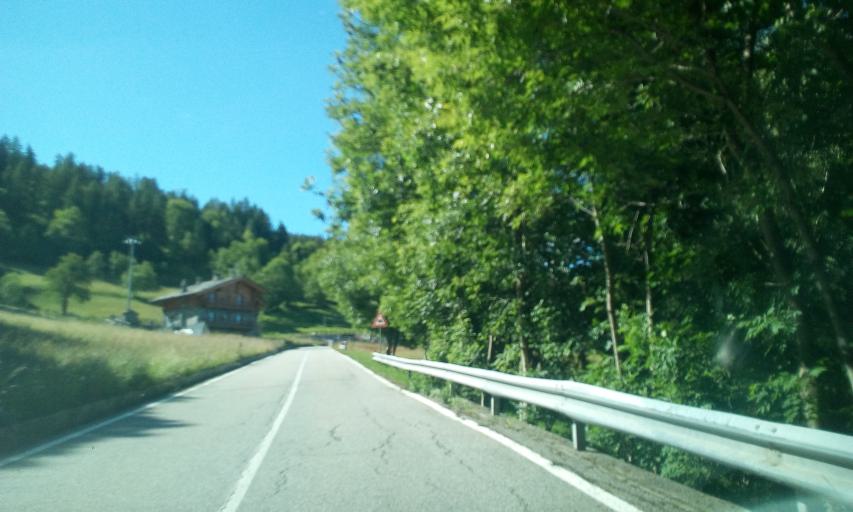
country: IT
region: Aosta Valley
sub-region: Valle d'Aosta
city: Emarese
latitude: 45.7513
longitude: 7.6903
